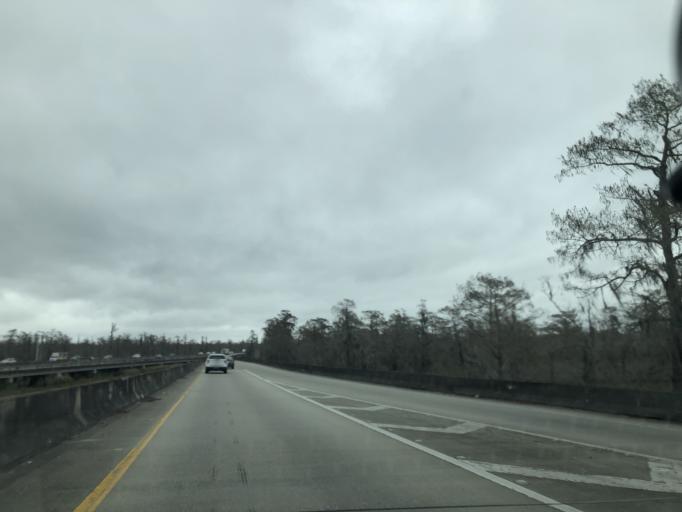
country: US
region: Louisiana
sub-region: Saint Charles Parish
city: Ama
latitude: 29.9778
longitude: -90.3148
